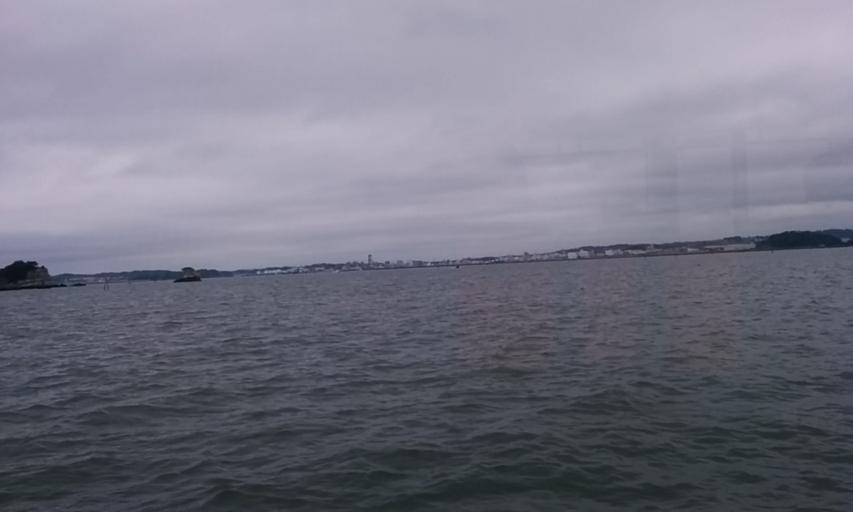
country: JP
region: Miyagi
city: Matsushima
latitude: 38.3343
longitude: 141.0729
